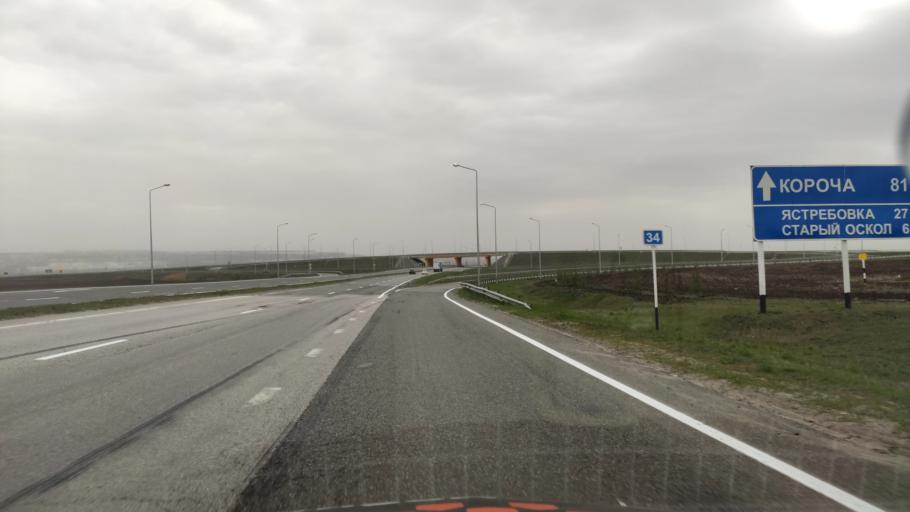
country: RU
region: Belgorod
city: Staryy Oskol
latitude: 51.3285
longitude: 37.7461
